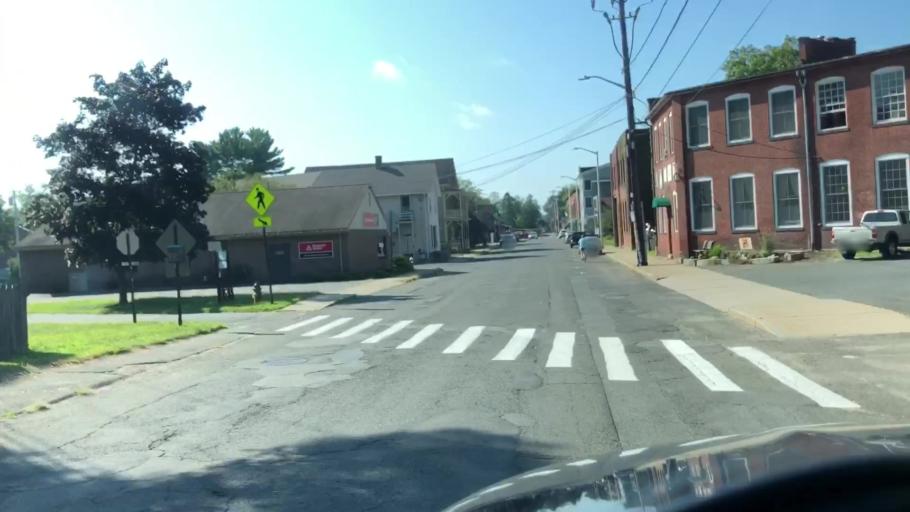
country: US
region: Massachusetts
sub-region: Hampshire County
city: Northampton
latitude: 42.3372
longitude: -72.6720
